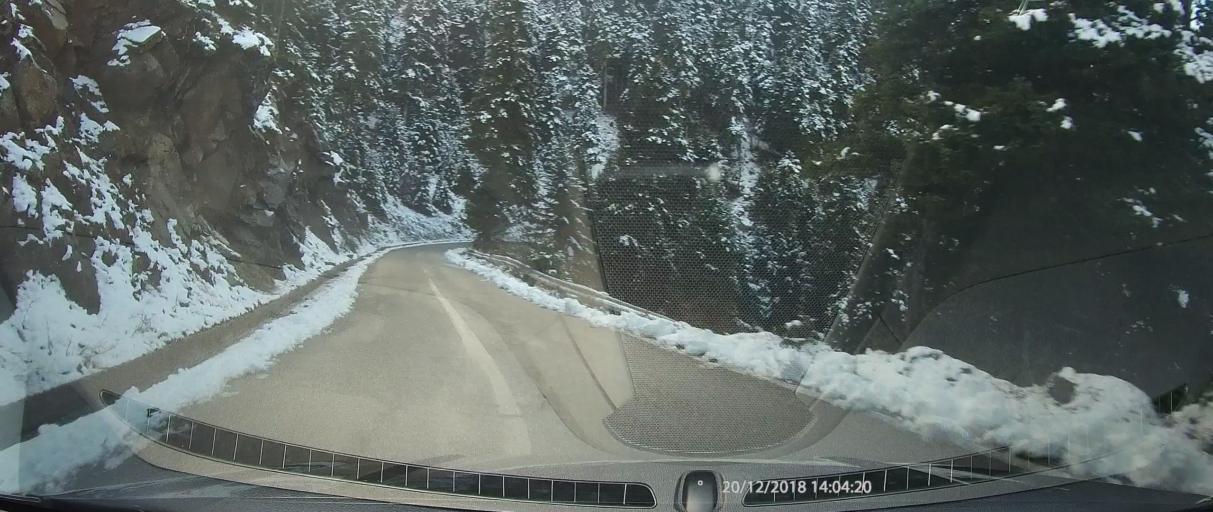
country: GR
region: West Greece
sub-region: Nomos Aitolias kai Akarnanias
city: Thermo
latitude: 38.7433
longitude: 21.6408
